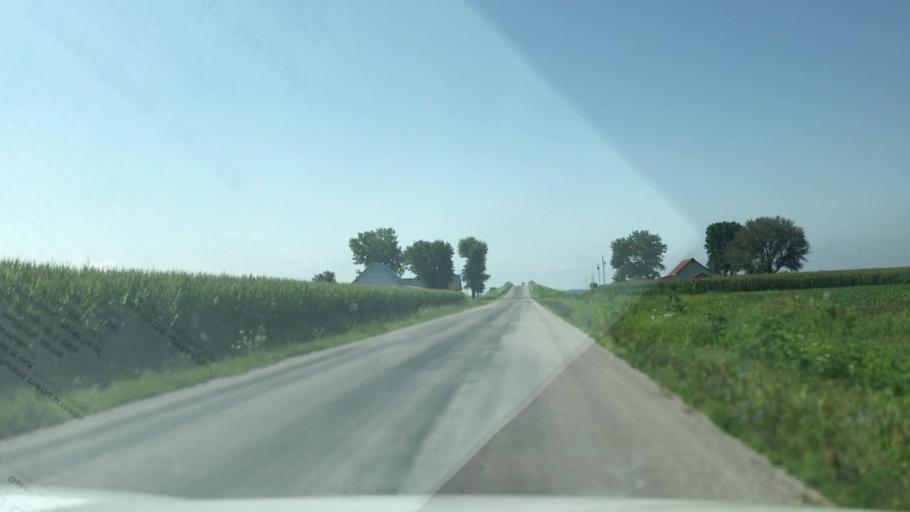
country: US
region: Illinois
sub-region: Washington County
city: Okawville
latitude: 38.4321
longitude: -89.4779
